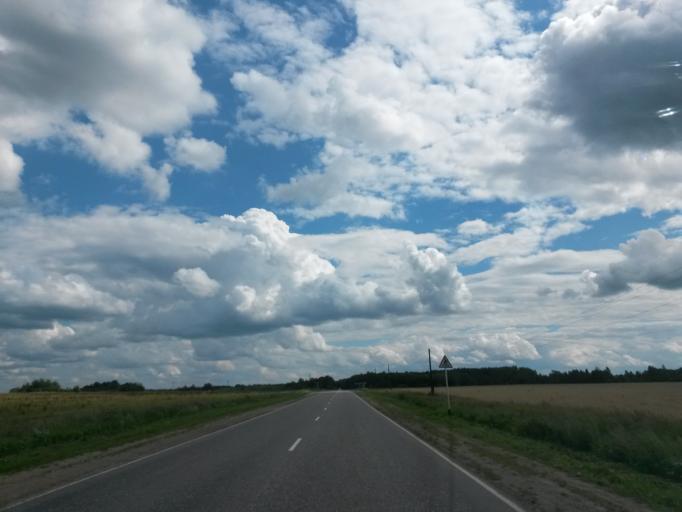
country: RU
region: Ivanovo
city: Pistsovo
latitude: 57.1299
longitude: 40.5980
